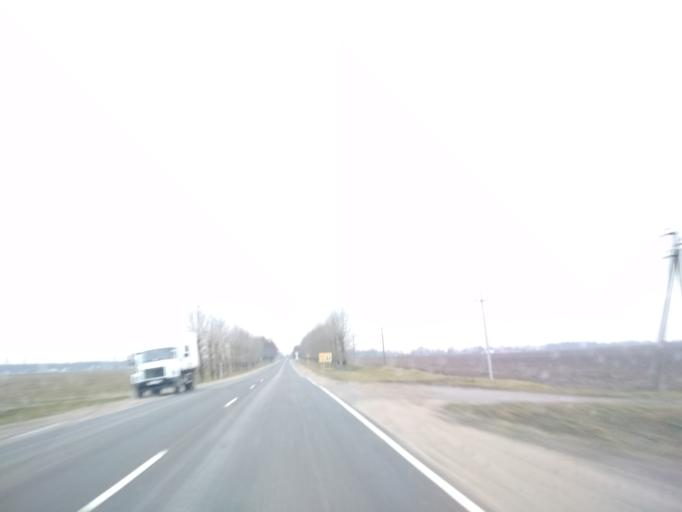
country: BY
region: Minsk
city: Blon'
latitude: 53.5360
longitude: 28.1572
